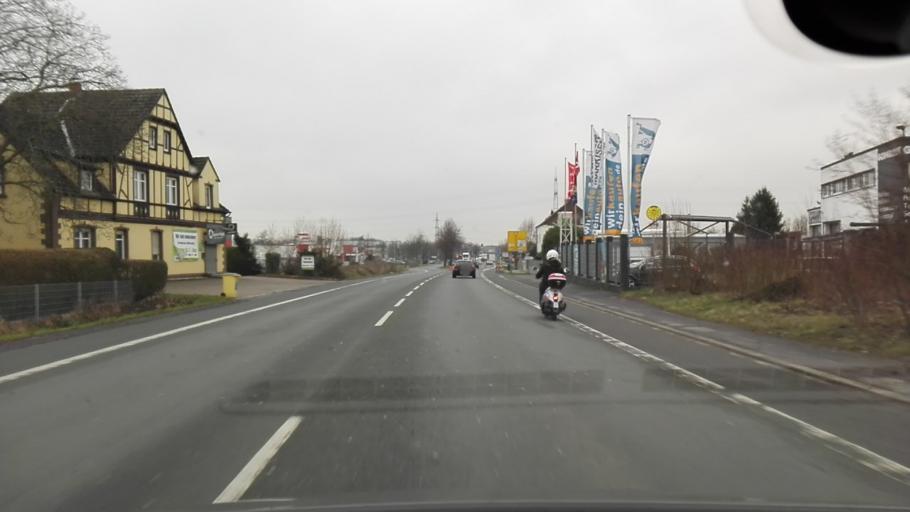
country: DE
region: North Rhine-Westphalia
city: Kamen
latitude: 51.5672
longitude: 7.6760
